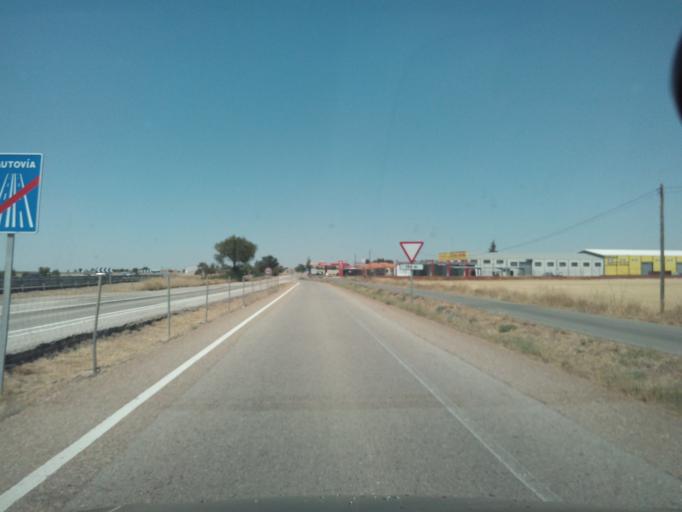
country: ES
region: Castille-La Mancha
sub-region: Province of Toledo
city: Tembleque
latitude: 39.7759
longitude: -3.4787
